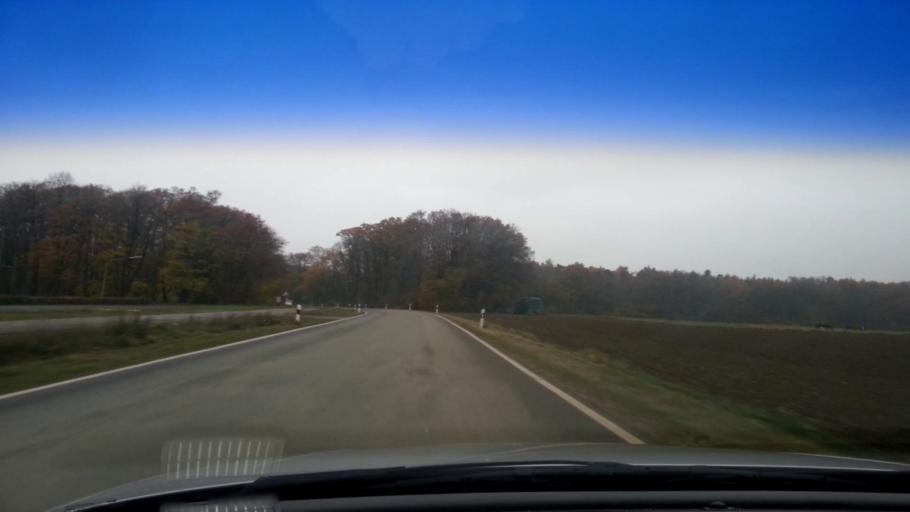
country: DE
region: Bavaria
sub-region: Upper Franconia
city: Litzendorf
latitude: 49.9282
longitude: 11.0014
